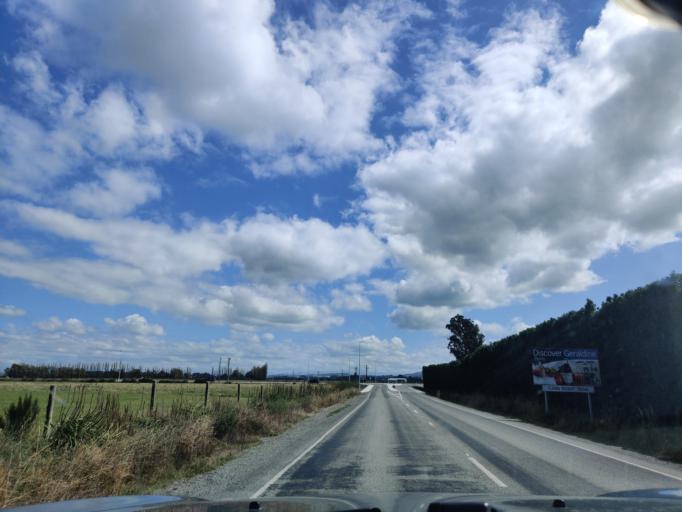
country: NZ
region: Canterbury
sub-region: Timaru District
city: Pleasant Point
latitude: -44.1261
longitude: 171.2527
